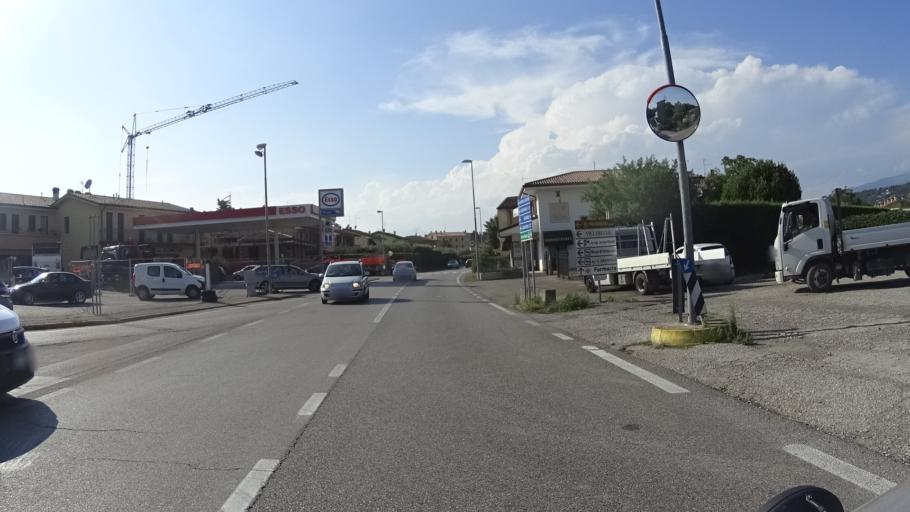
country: IT
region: Veneto
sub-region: Provincia di Verona
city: Calmasino
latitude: 45.5197
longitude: 10.7579
